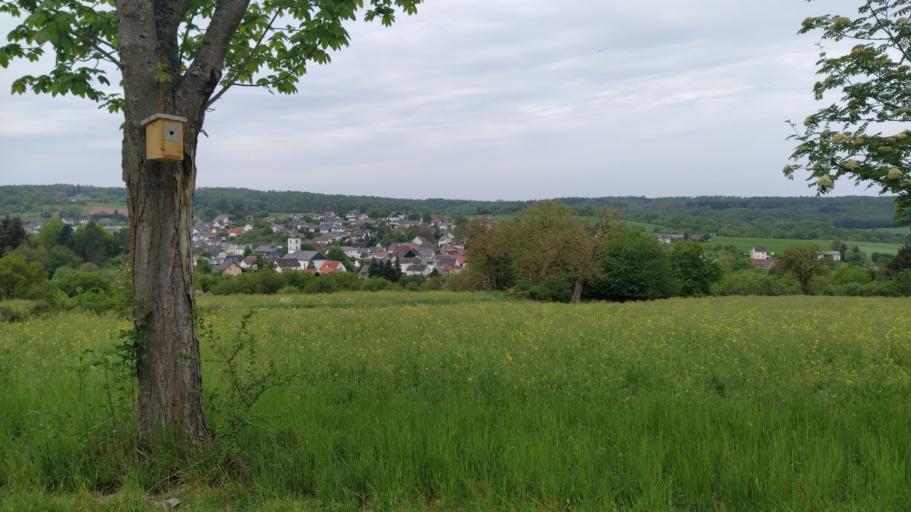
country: DE
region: Hesse
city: Weilmunster
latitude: 50.4660
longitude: 8.4133
